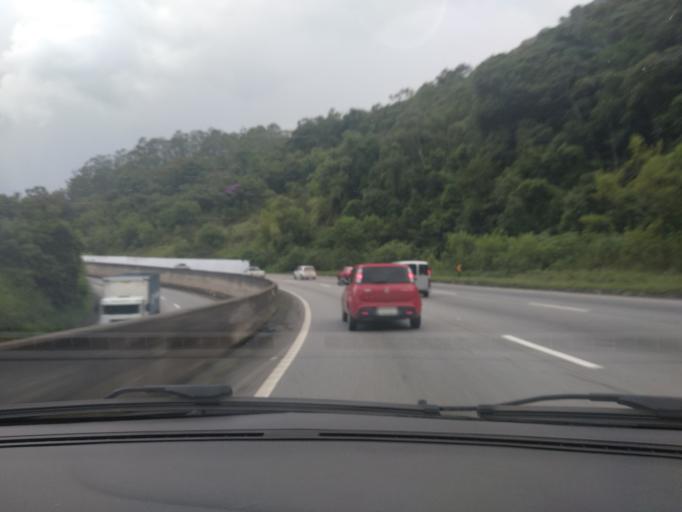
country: BR
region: Sao Paulo
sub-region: Mogi das Cruzes
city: Mogi das Cruzes
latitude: -23.4908
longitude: -46.2322
